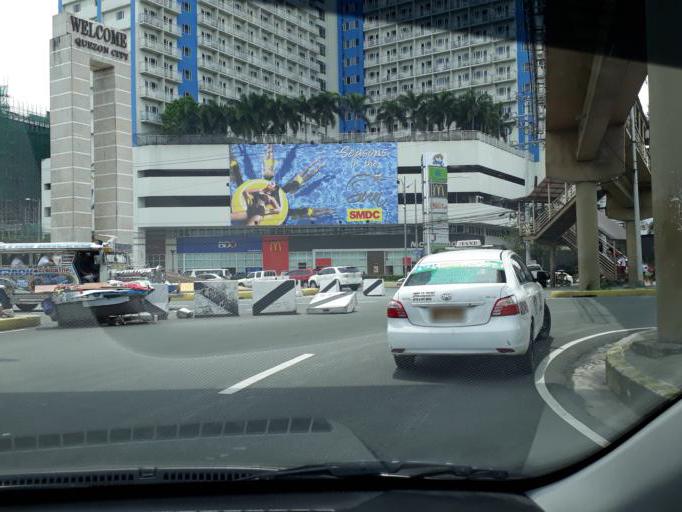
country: PH
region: Metro Manila
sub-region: City of Manila
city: Manila
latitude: 14.6179
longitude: 121.0024
